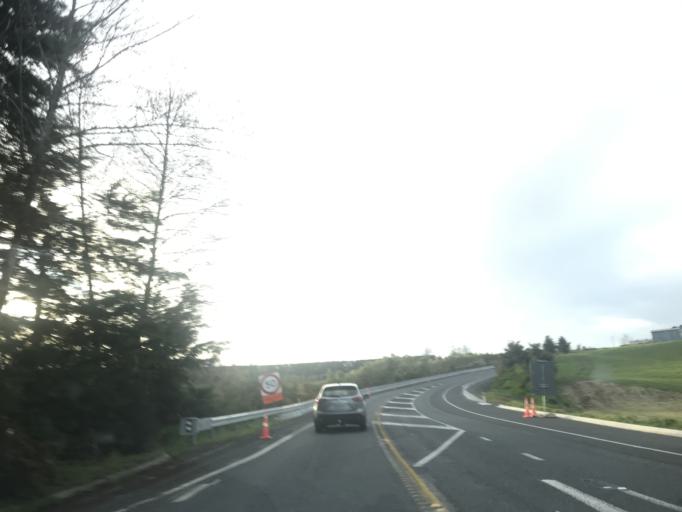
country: NZ
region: Bay of Plenty
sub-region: Western Bay of Plenty District
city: Waihi Beach
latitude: -37.4509
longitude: 175.8796
